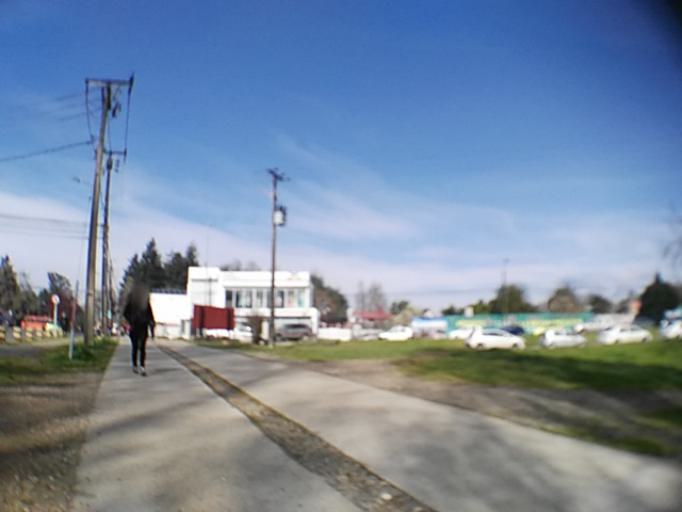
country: CL
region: Los Rios
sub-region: Provincia de Valdivia
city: Valdivia
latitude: -39.8098
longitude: -73.2520
